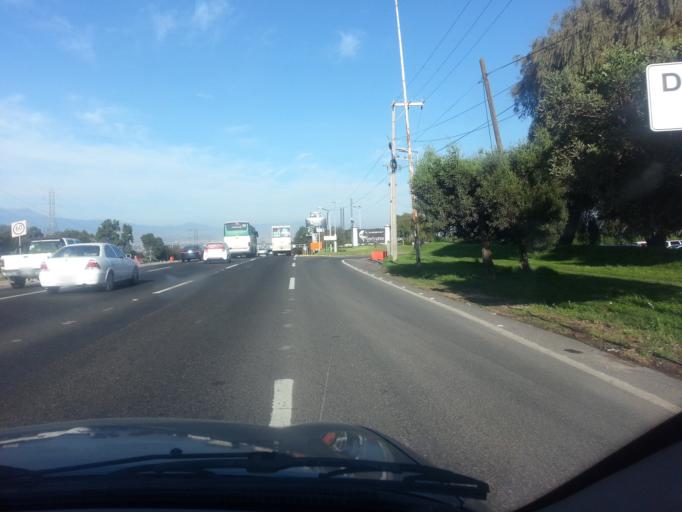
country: MX
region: Mexico
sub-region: Lerma
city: Fraccionamiento y Club de Golf los Encinos
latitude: 19.2832
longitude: -99.4727
